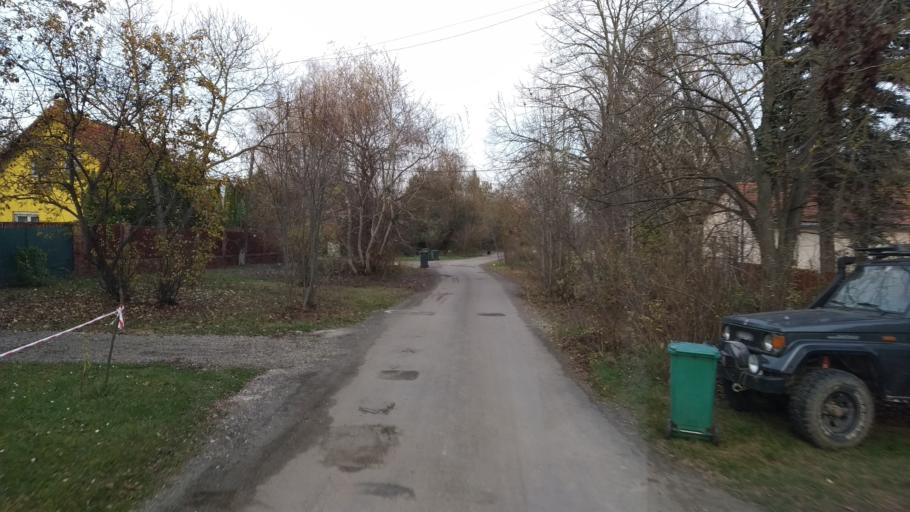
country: HU
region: Pest
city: God
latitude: 47.6837
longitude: 19.1138
